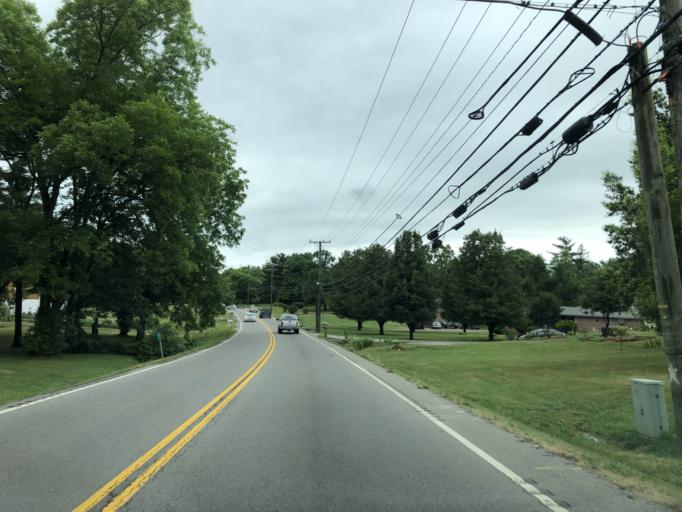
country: US
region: Tennessee
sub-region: Davidson County
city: Goodlettsville
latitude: 36.2750
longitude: -86.7646
